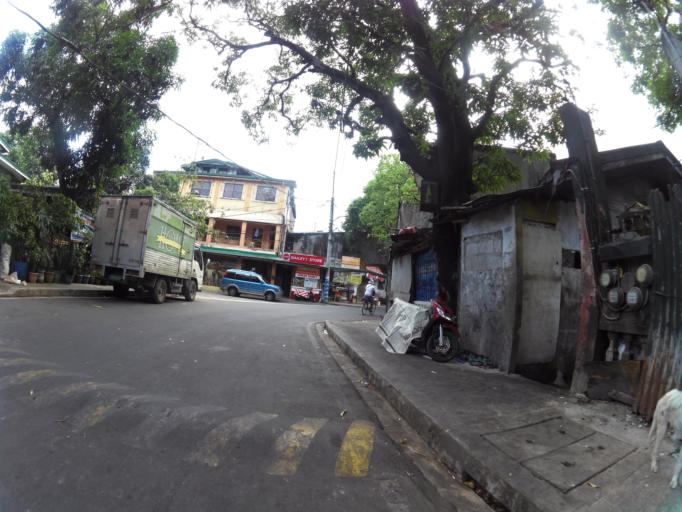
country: PH
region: Metro Manila
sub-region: Marikina
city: Calumpang
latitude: 14.6279
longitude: 121.1051
